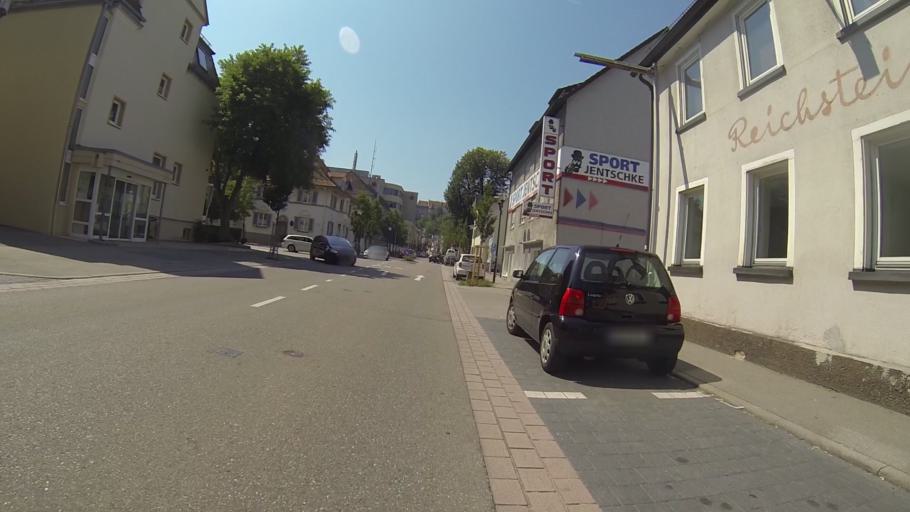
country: DE
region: Baden-Wuerttemberg
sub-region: Regierungsbezirk Stuttgart
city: Heidenheim an der Brenz
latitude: 48.6815
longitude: 10.1526
